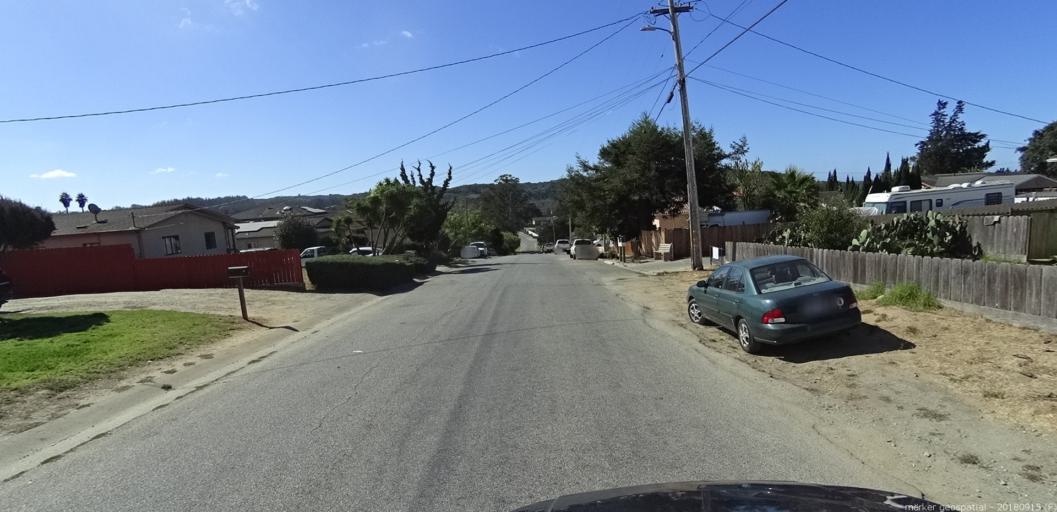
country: US
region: California
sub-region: Monterey County
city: Las Lomas
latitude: 36.8702
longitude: -121.7307
